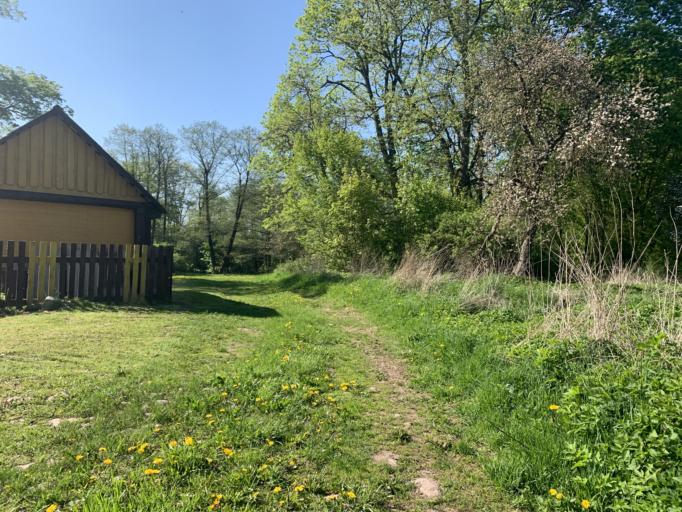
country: BY
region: Minsk
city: Kapyl'
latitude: 53.2592
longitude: 26.9497
